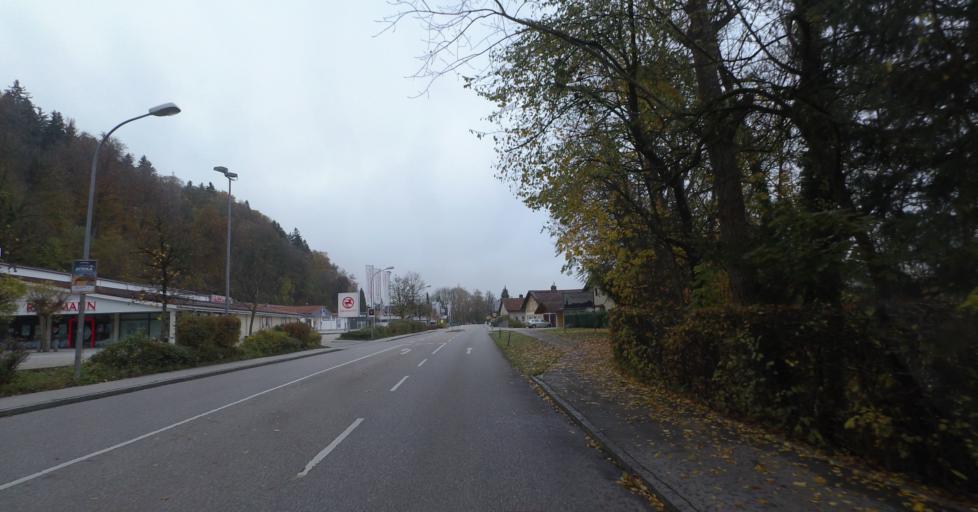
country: DE
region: Bavaria
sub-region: Upper Bavaria
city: Trostberg an der Alz
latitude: 48.0332
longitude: 12.5581
